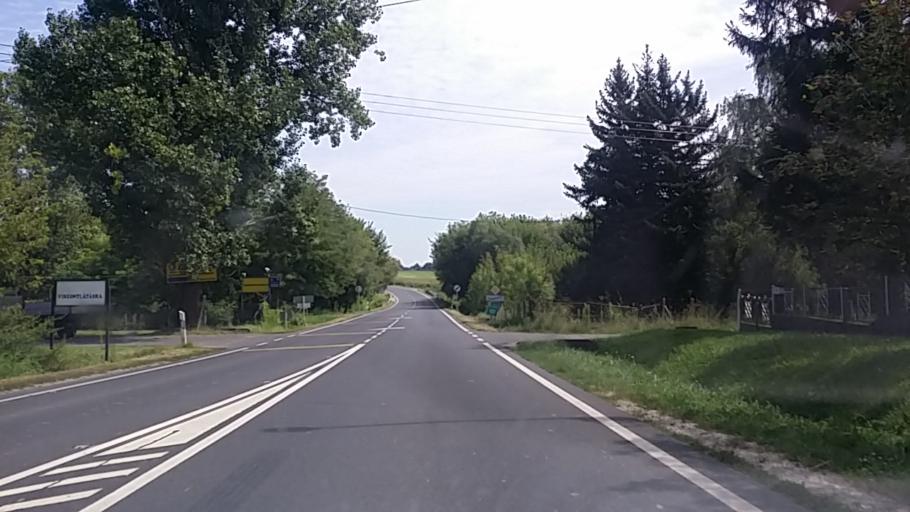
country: HU
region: Somogy
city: Taszar
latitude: 46.3646
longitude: 18.0134
